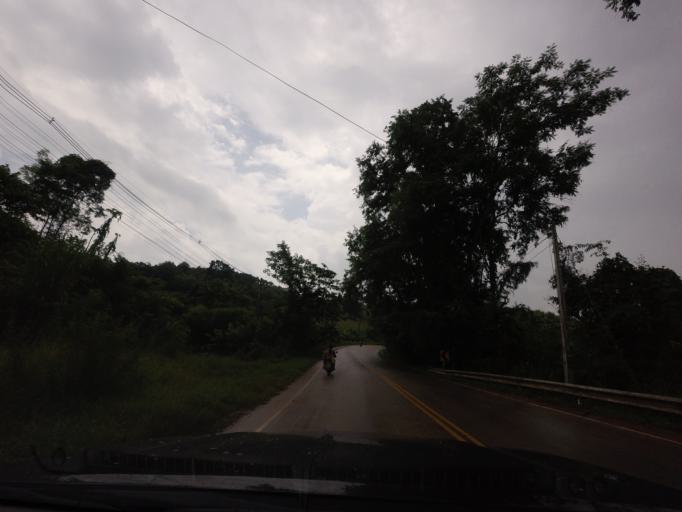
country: TH
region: Loei
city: Pak Chom
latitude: 18.1232
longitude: 102.0005
